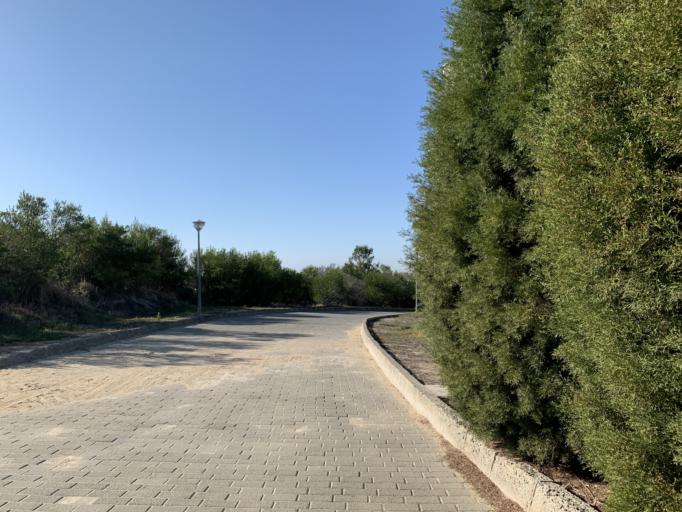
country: CY
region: Larnaka
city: Larnaca
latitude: 34.9055
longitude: 33.6250
